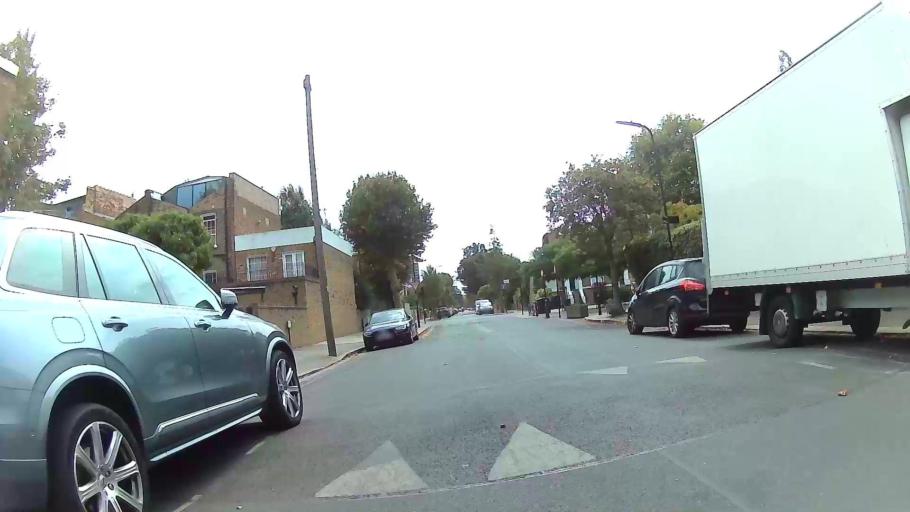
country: GB
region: England
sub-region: Greater London
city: Islington
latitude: 51.5432
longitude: -0.0814
